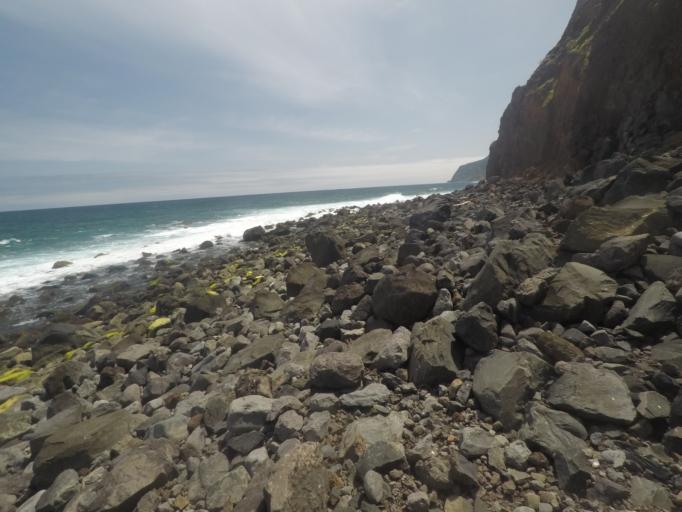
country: PT
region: Madeira
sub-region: Sao Vicente
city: Sao Vicente
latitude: 32.8302
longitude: -16.9896
